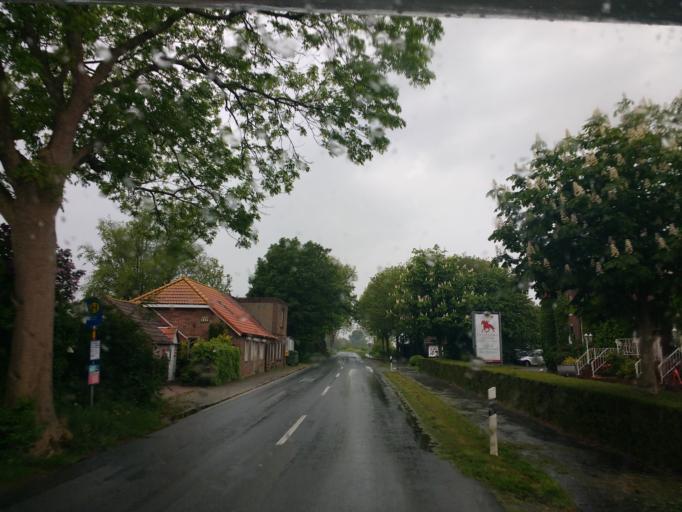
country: DE
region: Lower Saxony
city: Schillig
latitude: 53.7048
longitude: 7.9856
